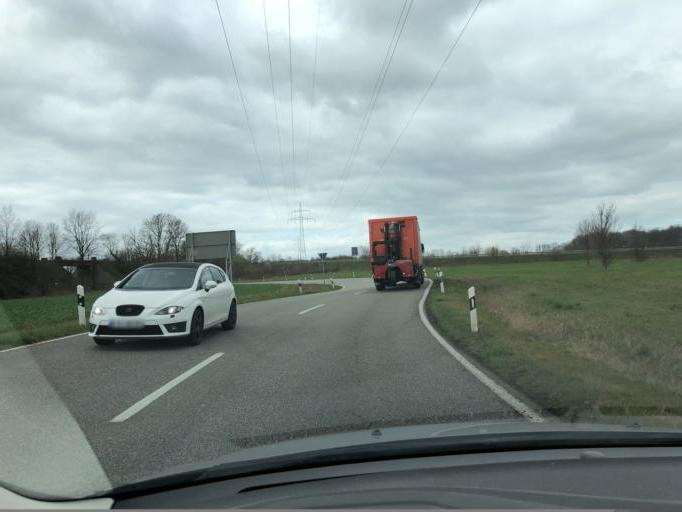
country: DE
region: Saxony-Anhalt
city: Zeitz
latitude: 51.0814
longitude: 12.1645
